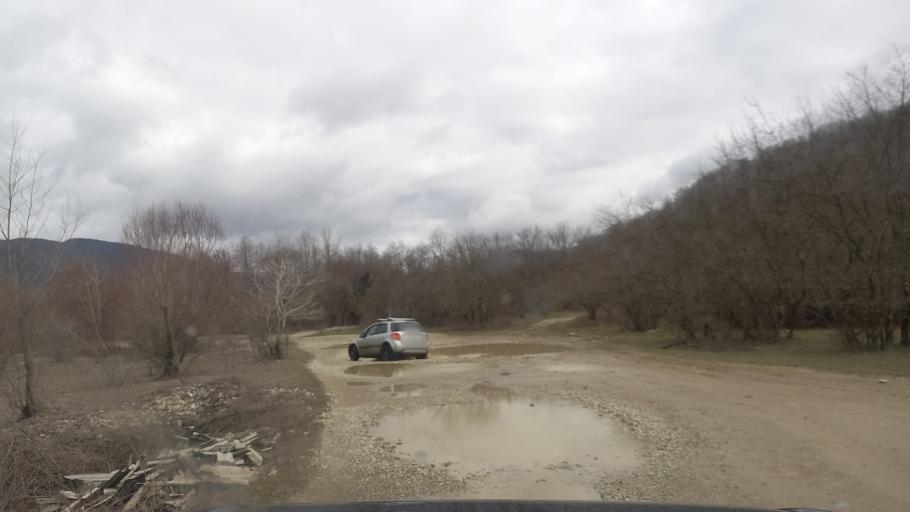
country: RU
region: Krasnodarskiy
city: Pshada
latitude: 44.4834
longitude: 38.4084
